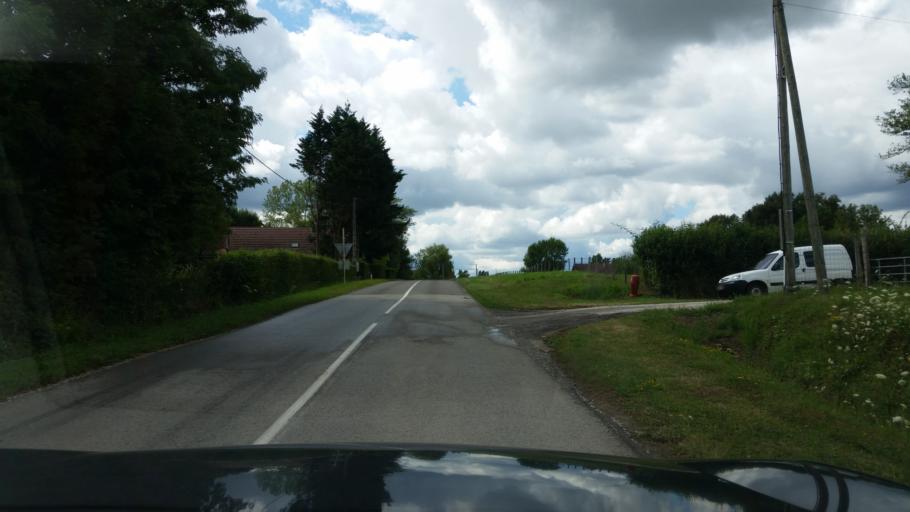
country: FR
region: Bourgogne
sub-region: Departement de Saone-et-Loire
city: Saint-Usuge
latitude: 46.7161
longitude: 5.3119
